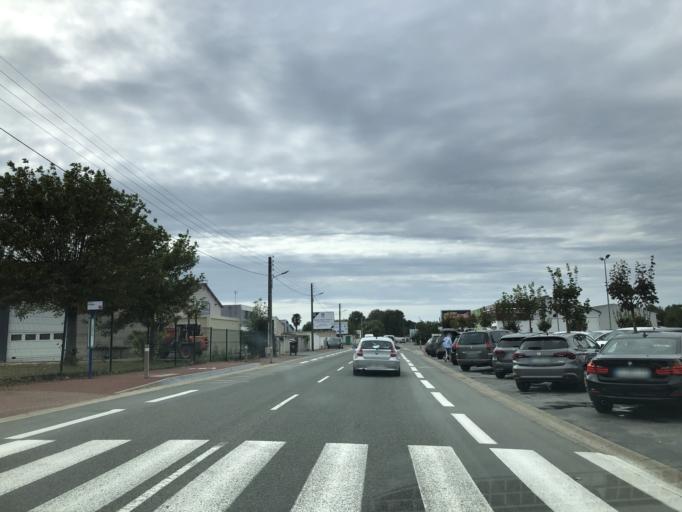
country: FR
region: Poitou-Charentes
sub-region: Departement de la Charente-Maritime
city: Saint-Georges-de-Didonne
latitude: 45.6309
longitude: -0.9991
